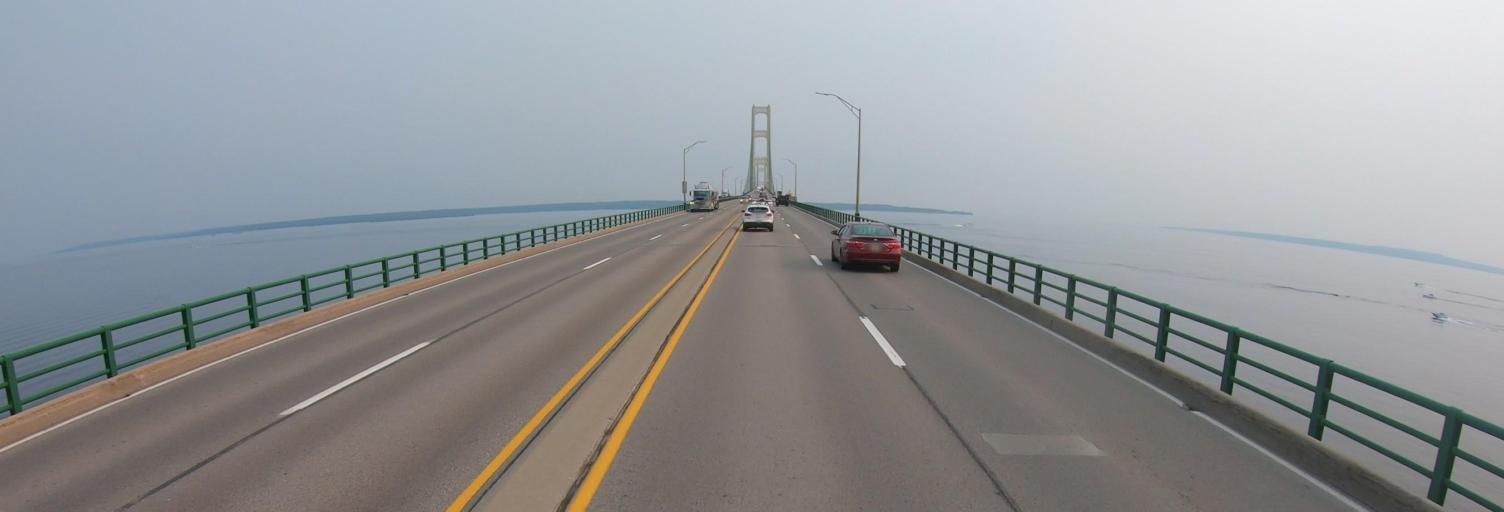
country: US
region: Michigan
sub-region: Mackinac County
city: Saint Ignace
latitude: 45.8022
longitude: -84.7321
